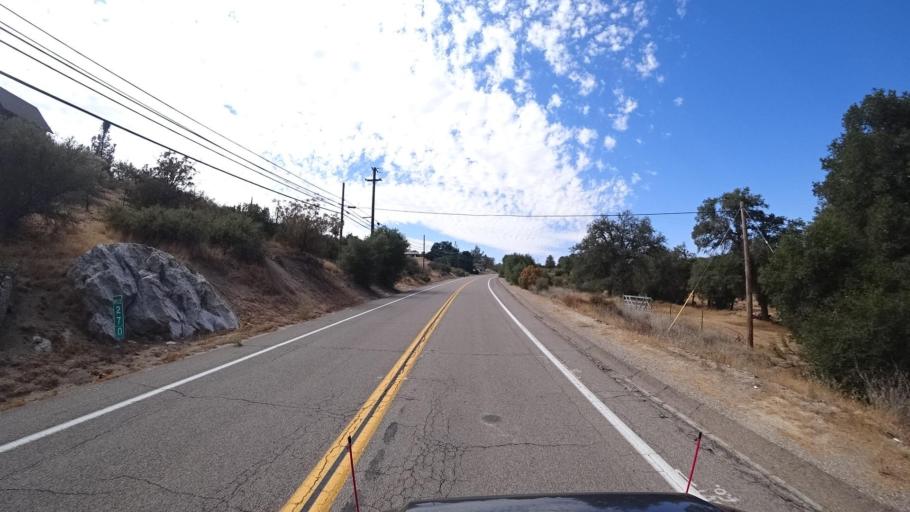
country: MX
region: Baja California
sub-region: Tecate
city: Cereso del Hongo
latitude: 32.6662
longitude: -116.2832
